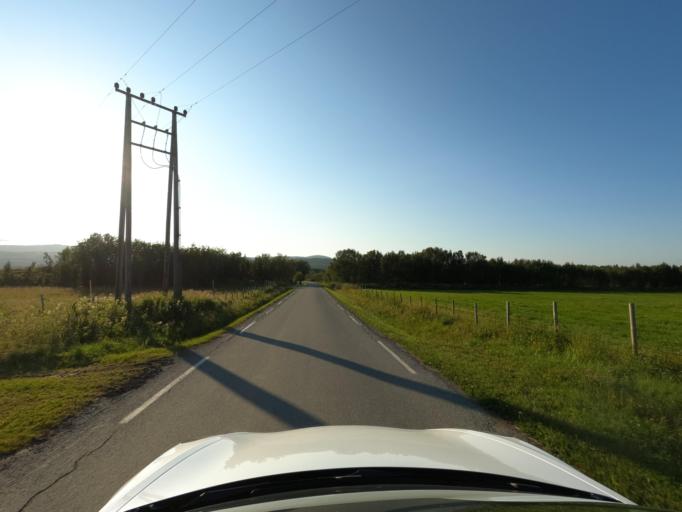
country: NO
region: Troms
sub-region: Skanland
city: Evenskjer
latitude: 68.4620
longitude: 16.6774
